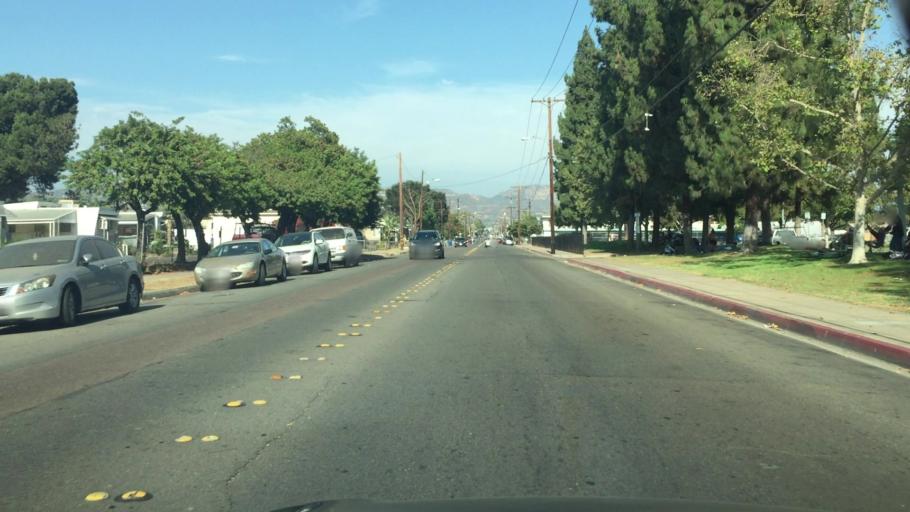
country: US
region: California
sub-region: San Diego County
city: Bostonia
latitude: 32.8002
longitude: -116.9431
